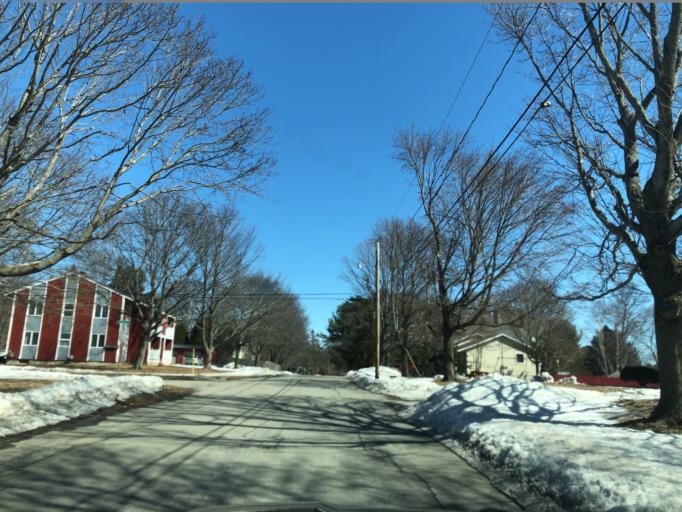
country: US
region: Maine
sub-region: Penobscot County
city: Brewer
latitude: 44.8161
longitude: -68.7564
